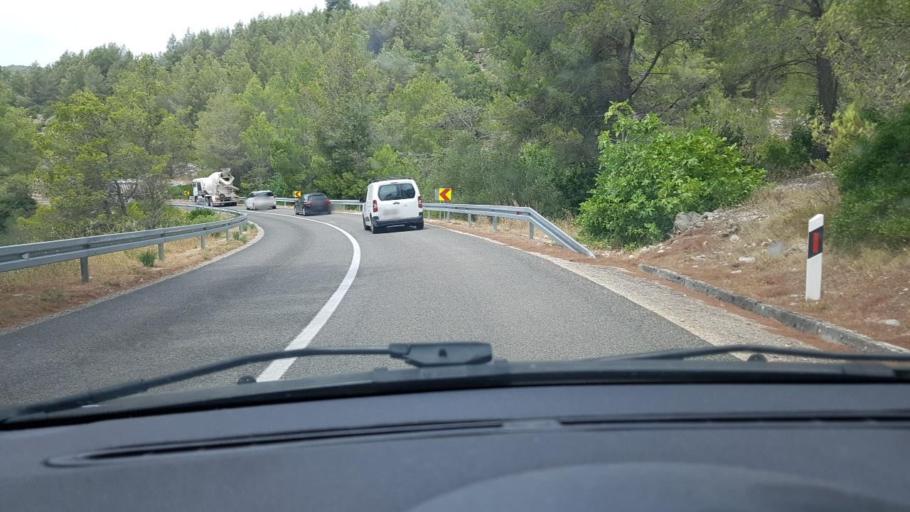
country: HR
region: Dubrovacko-Neretvanska
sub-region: Grad Dubrovnik
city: Vela Luka
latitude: 42.9501
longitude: 16.7909
